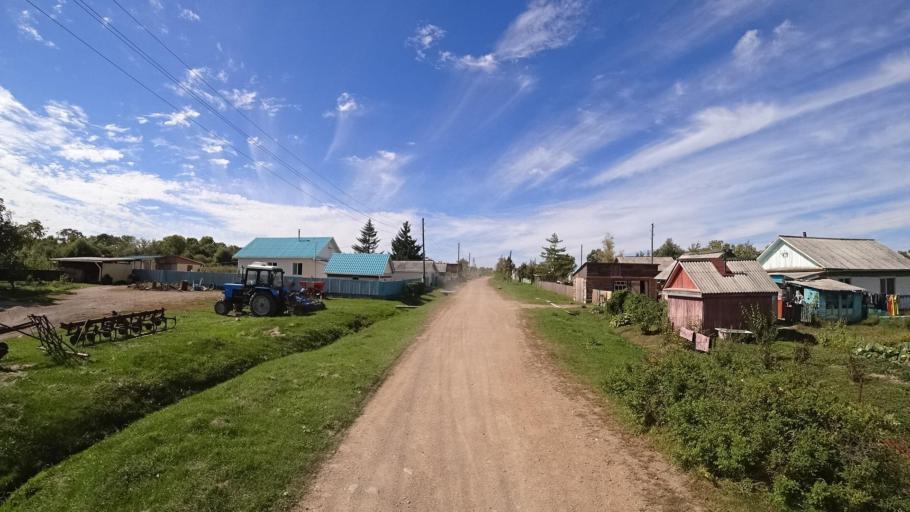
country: RU
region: Primorskiy
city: Yakovlevka
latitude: 44.4292
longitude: 133.5649
